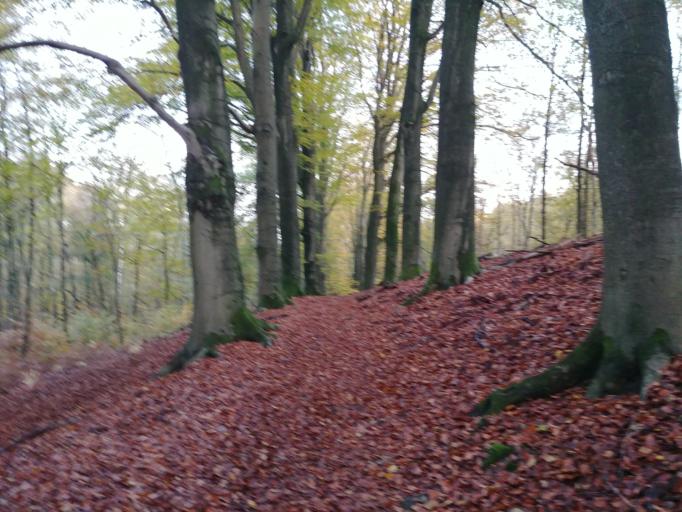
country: NL
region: Gelderland
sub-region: Gemeente Rheden
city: De Steeg
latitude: 52.0408
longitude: 6.0396
